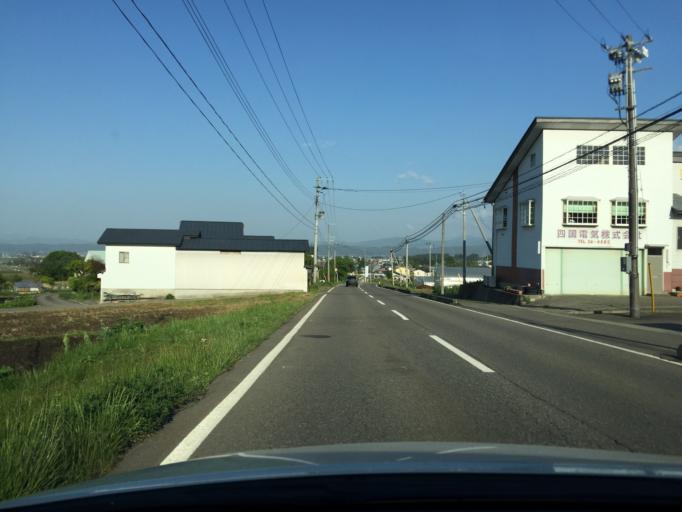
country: JP
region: Fukushima
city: Kitakata
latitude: 37.6548
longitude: 139.9359
